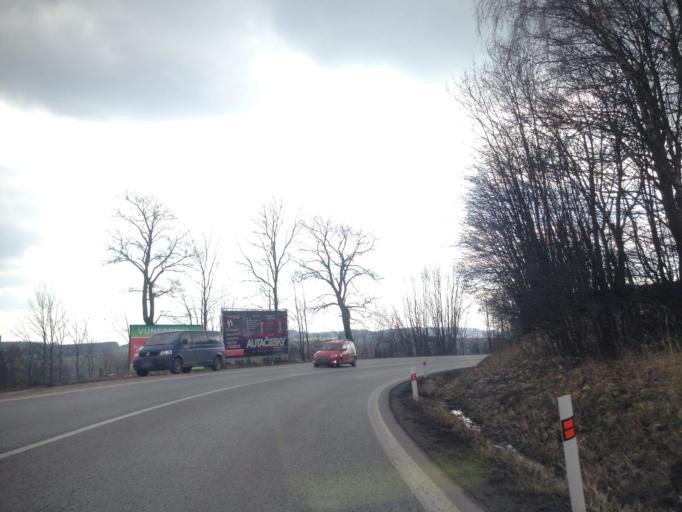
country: CZ
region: Liberecky
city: Studenec
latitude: 50.5172
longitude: 15.5643
